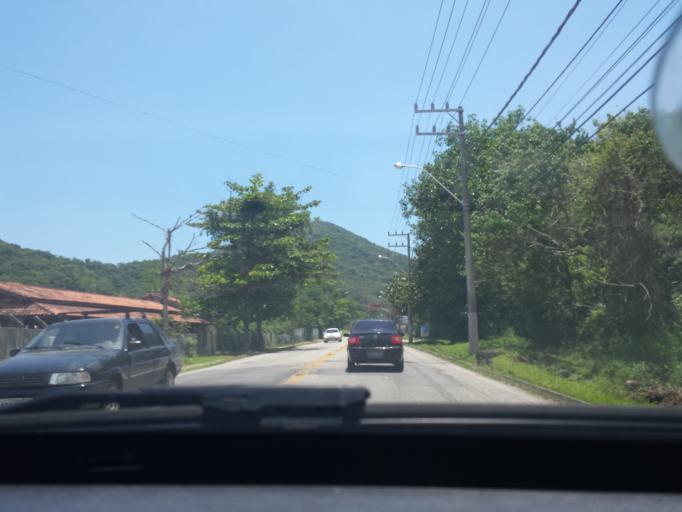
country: BR
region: Santa Catarina
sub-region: Porto Belo
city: Porto Belo
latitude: -27.1455
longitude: -48.5316
